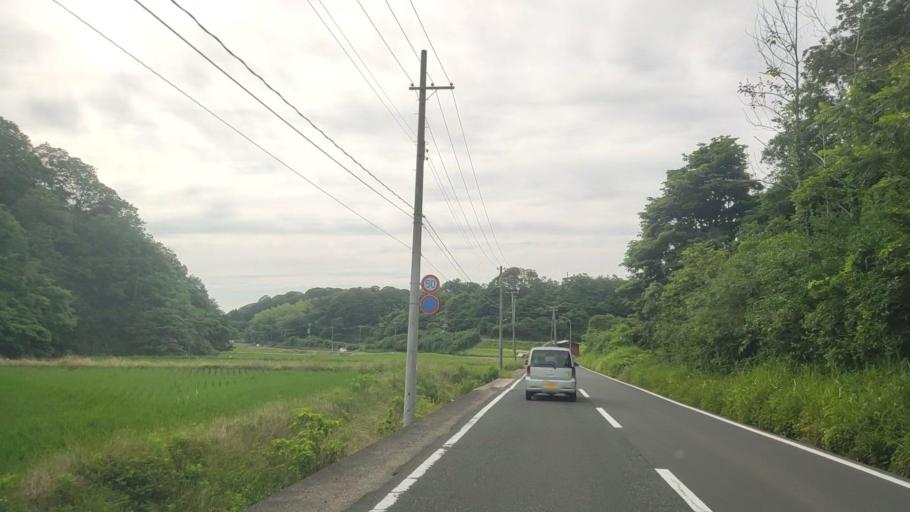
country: JP
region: Kyoto
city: Miyazu
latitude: 35.6823
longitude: 135.0669
